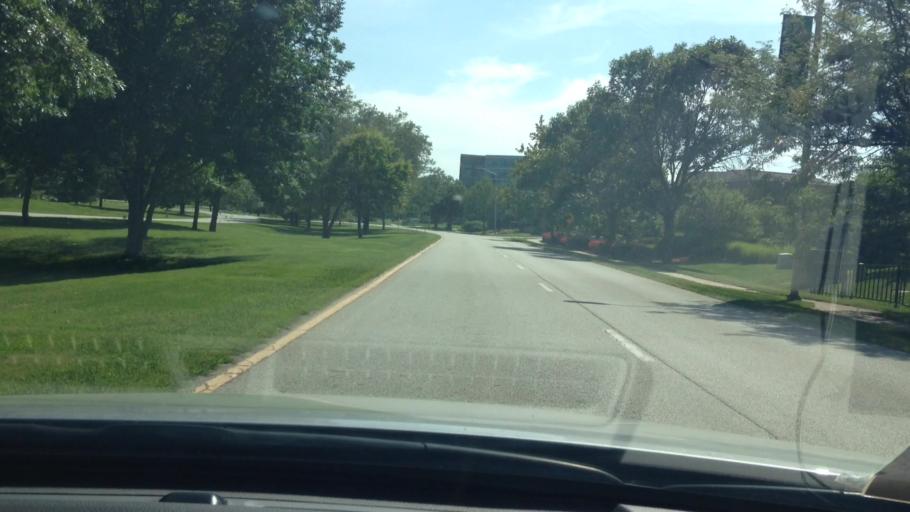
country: US
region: Kansas
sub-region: Johnson County
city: Leawood
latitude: 38.9251
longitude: -94.6266
